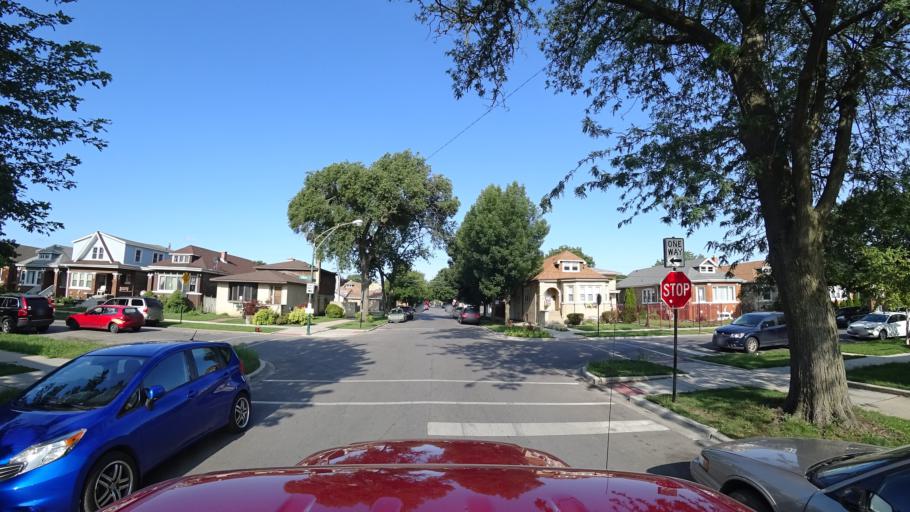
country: US
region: Illinois
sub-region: Cook County
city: Hometown
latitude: 41.7898
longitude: -87.7081
